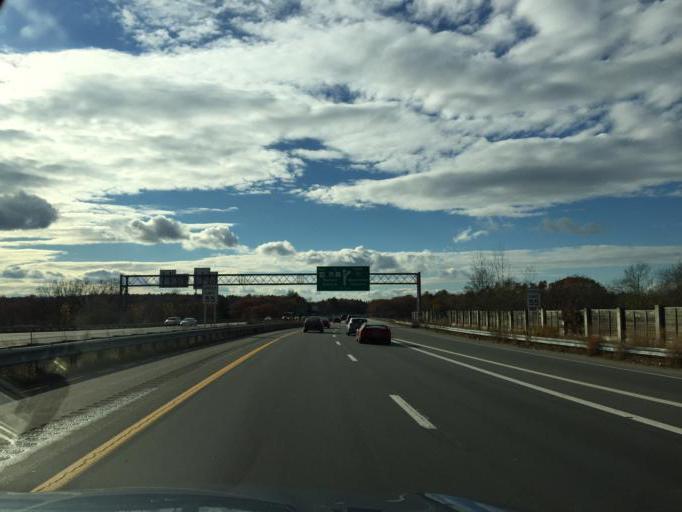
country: US
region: New Hampshire
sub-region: Hillsborough County
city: Manchester
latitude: 42.9480
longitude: -71.4574
